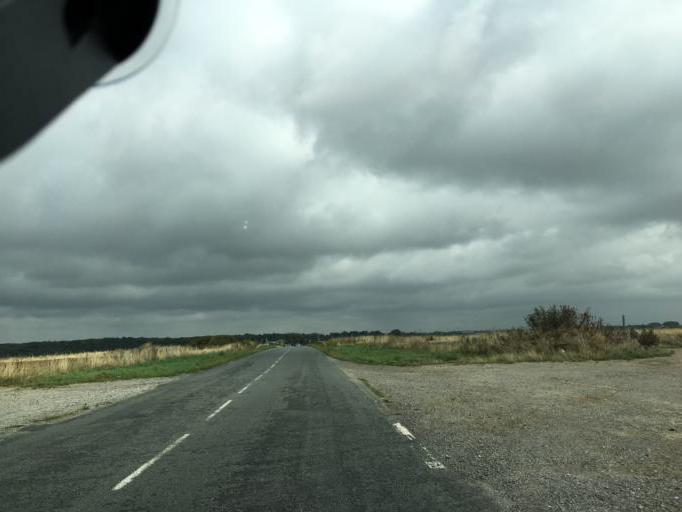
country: FR
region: Nord-Pas-de-Calais
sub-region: Departement du Pas-de-Calais
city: Rang-du-Fliers
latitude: 50.4266
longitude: 1.6920
